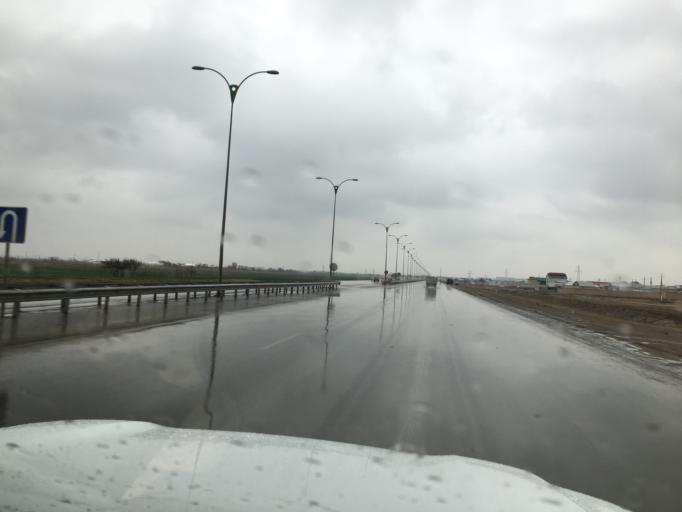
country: TM
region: Mary
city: Mary
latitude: 37.5608
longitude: 61.8490
